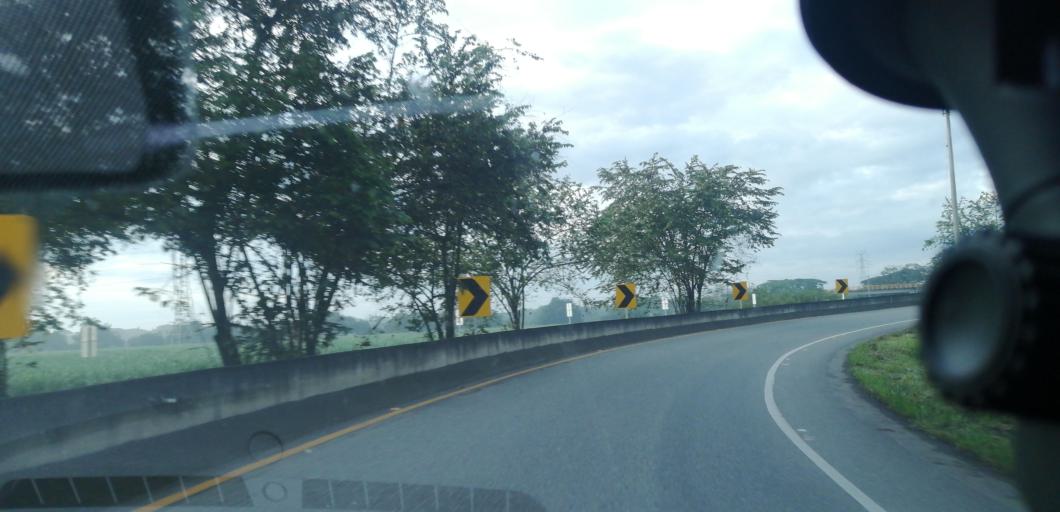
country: CO
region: Valle del Cauca
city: Palmira
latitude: 3.5238
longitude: -76.3363
